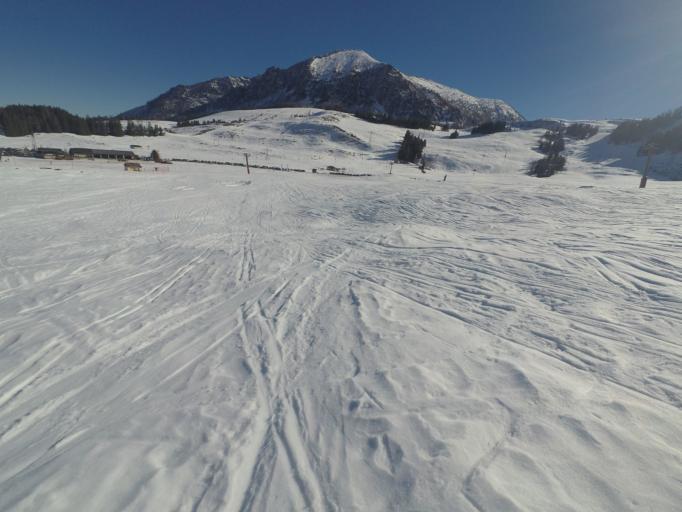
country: AT
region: Salzburg
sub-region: Politischer Bezirk Salzburg-Umgebung
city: Strobl
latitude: 47.6486
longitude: 13.4271
